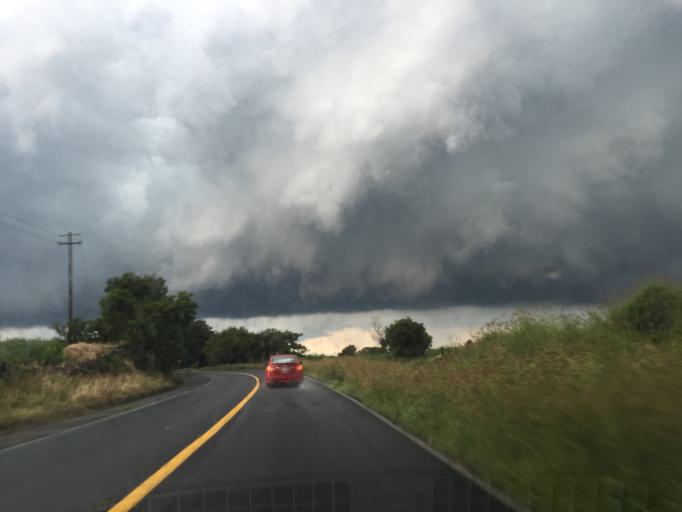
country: MX
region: Colima
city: Queseria
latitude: 19.3702
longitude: -103.5795
